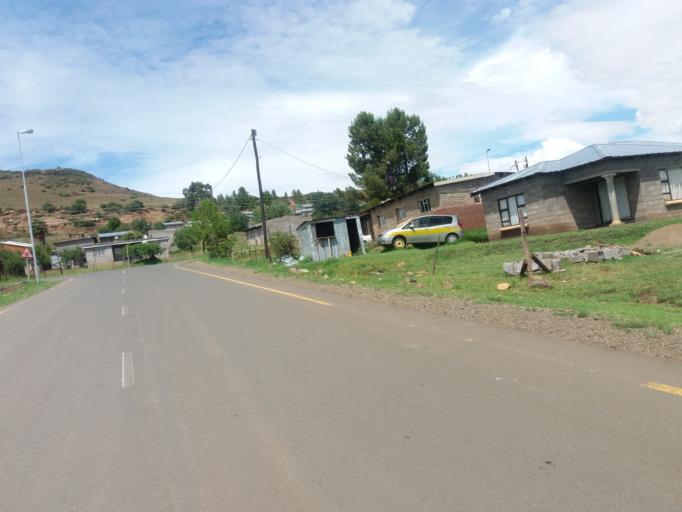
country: LS
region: Quthing
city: Quthing
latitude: -30.4105
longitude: 27.6958
